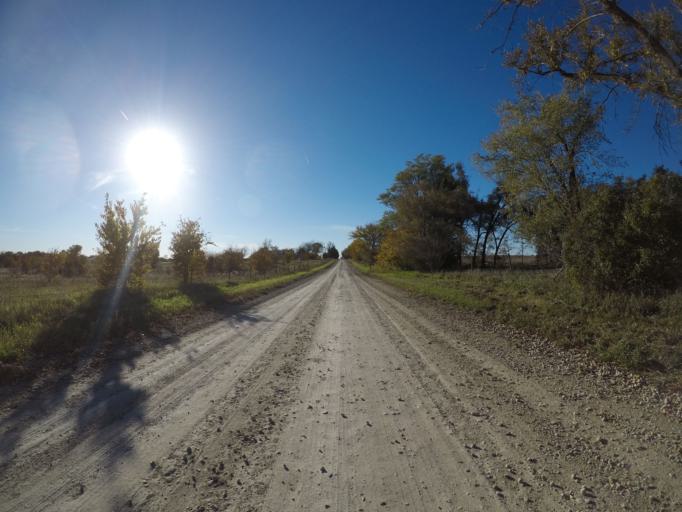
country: US
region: Kansas
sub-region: Riley County
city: Ogden
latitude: 39.2620
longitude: -96.7574
